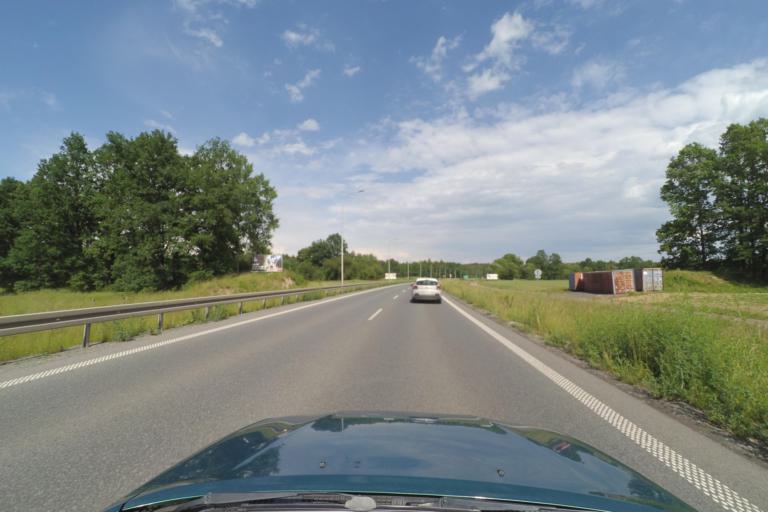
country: PL
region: Lower Silesian Voivodeship
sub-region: Powiat jeleniogorski
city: Janowice Wielkie
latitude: 50.9021
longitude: 15.8607
